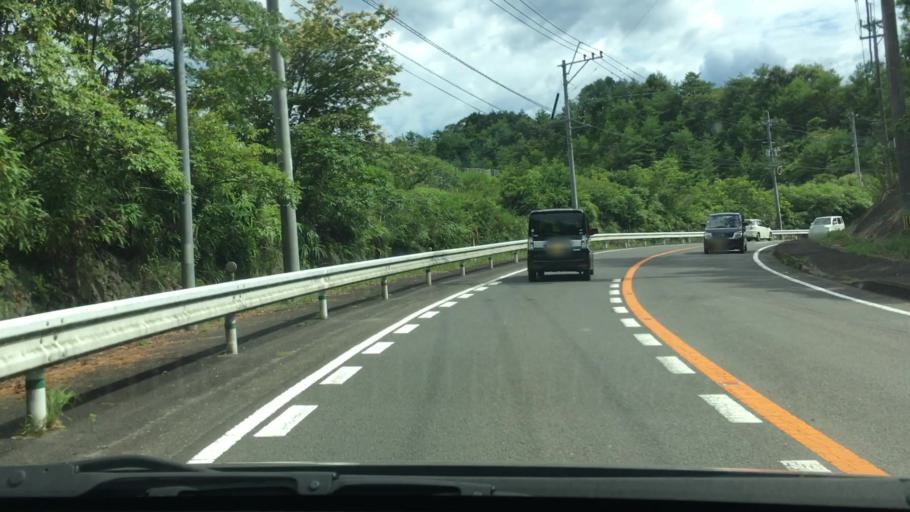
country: JP
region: Nagasaki
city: Togitsu
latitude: 32.9605
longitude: 129.7836
